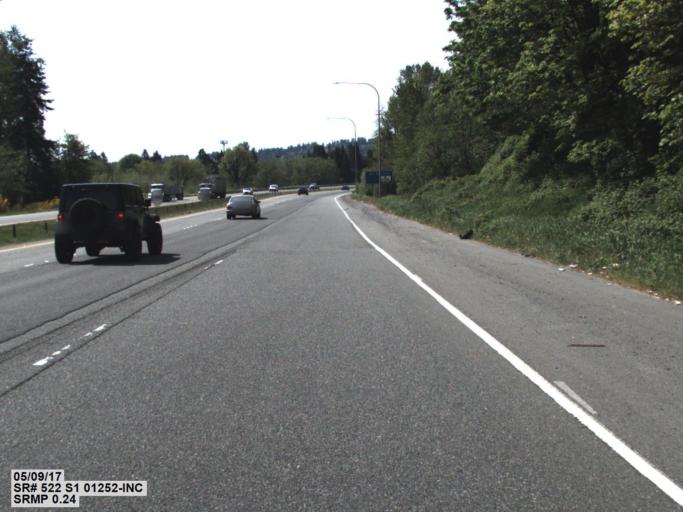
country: US
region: Washington
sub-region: King County
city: Seattle
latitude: 47.6816
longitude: -122.3194
